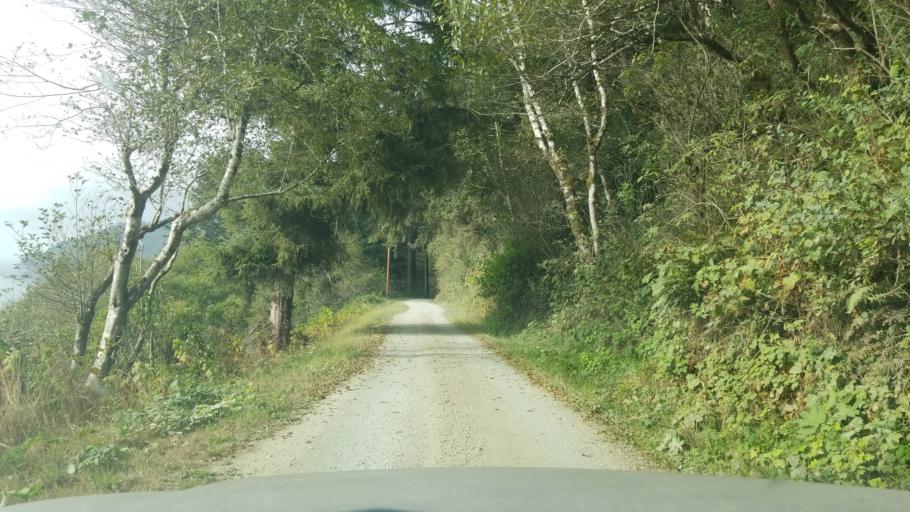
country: US
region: California
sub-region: Del Norte County
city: Bertsch-Oceanview
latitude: 41.5304
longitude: -124.0791
